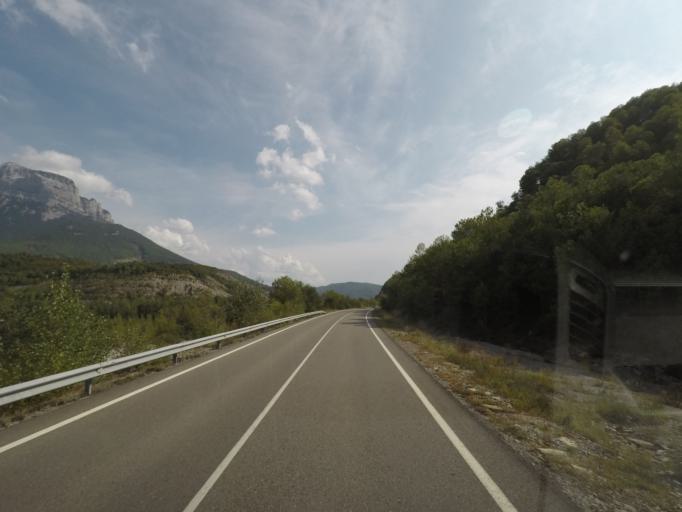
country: ES
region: Aragon
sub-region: Provincia de Huesca
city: Laspuna
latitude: 42.5150
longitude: 0.1434
